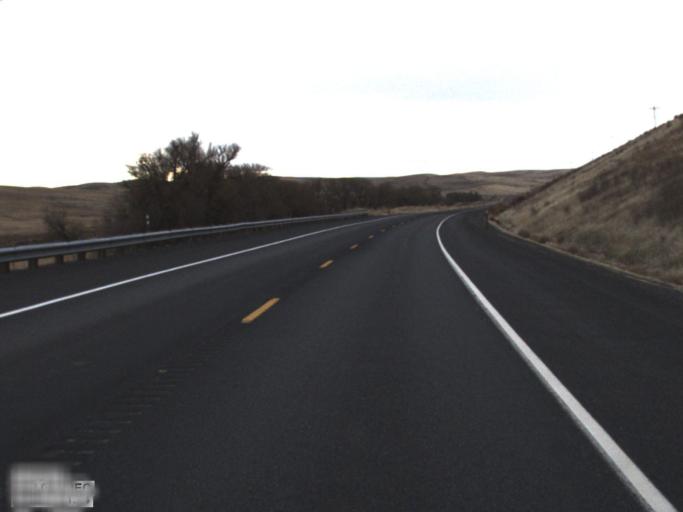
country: US
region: Washington
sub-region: Columbia County
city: Dayton
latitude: 46.7732
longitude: -117.9612
